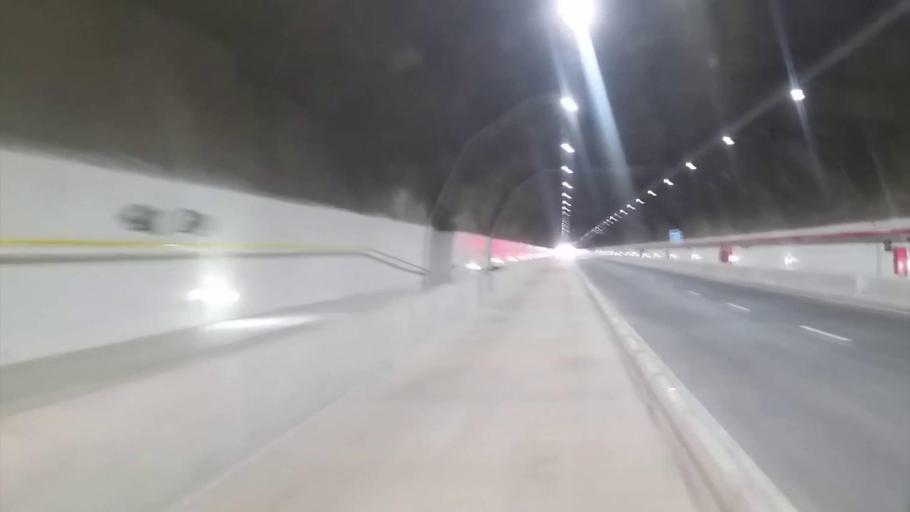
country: BR
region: Rio de Janeiro
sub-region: Nilopolis
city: Nilopolis
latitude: -22.8963
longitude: -43.3991
